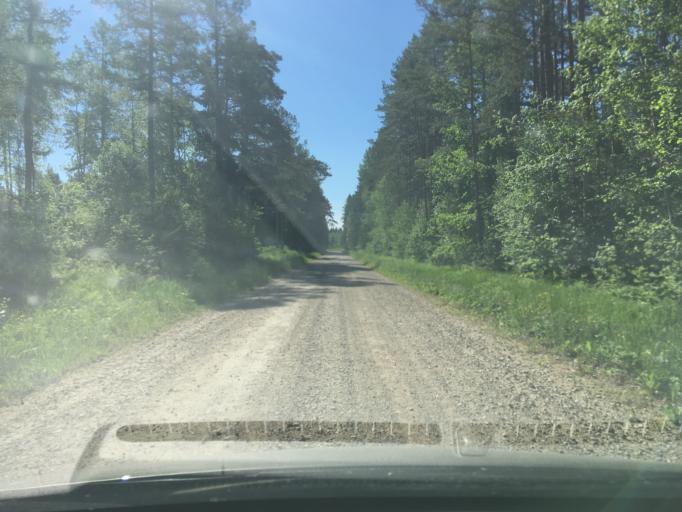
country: EE
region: Laeaene
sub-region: Lihula vald
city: Lihula
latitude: 58.6360
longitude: 23.7964
